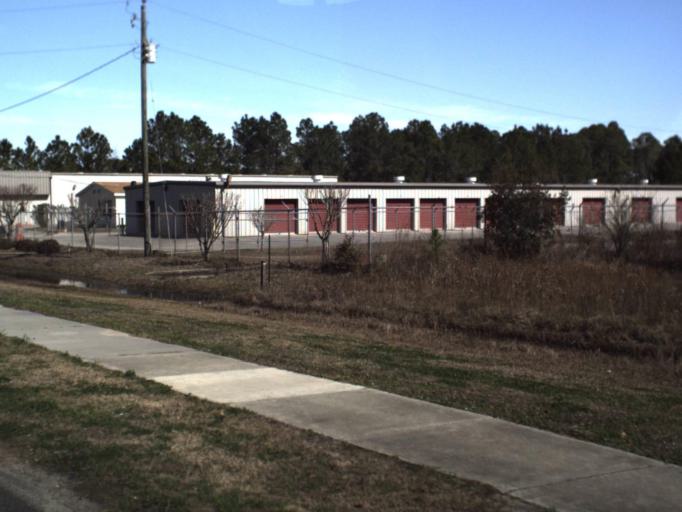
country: US
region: Florida
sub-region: Bay County
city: Hiland Park
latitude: 30.2083
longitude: -85.6495
